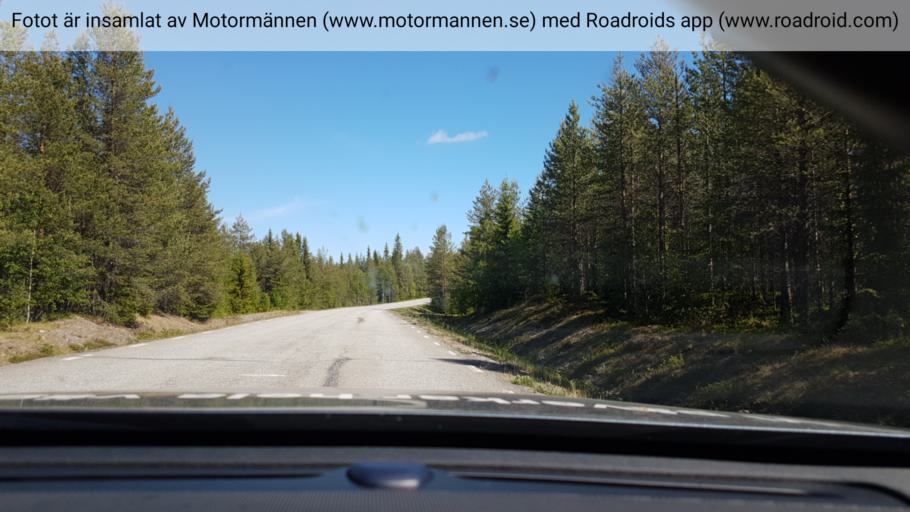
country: SE
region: Vaesterbotten
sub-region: Vilhelmina Kommun
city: Vilhelmina
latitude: 64.6265
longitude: 16.8527
